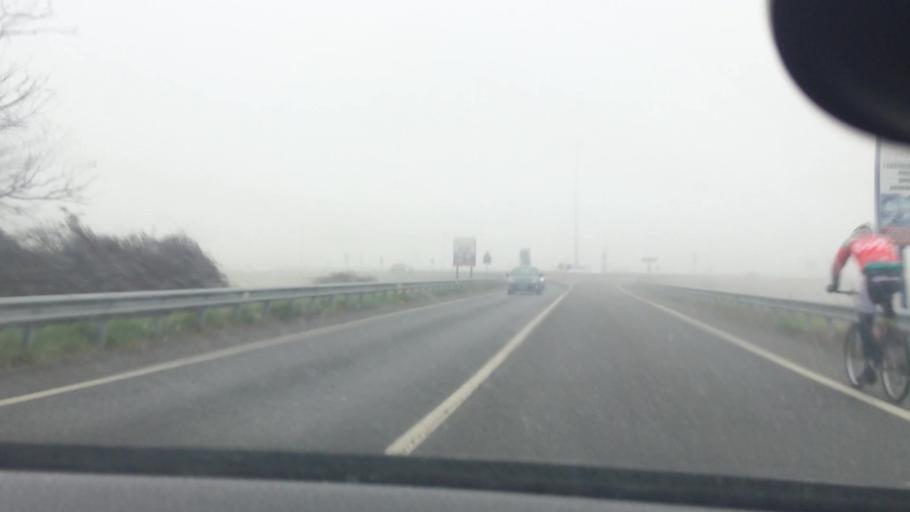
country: IT
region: Lombardy
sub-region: Provincia di Monza e Brianza
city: Ceriano Laghetto
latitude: 45.6281
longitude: 9.0603
